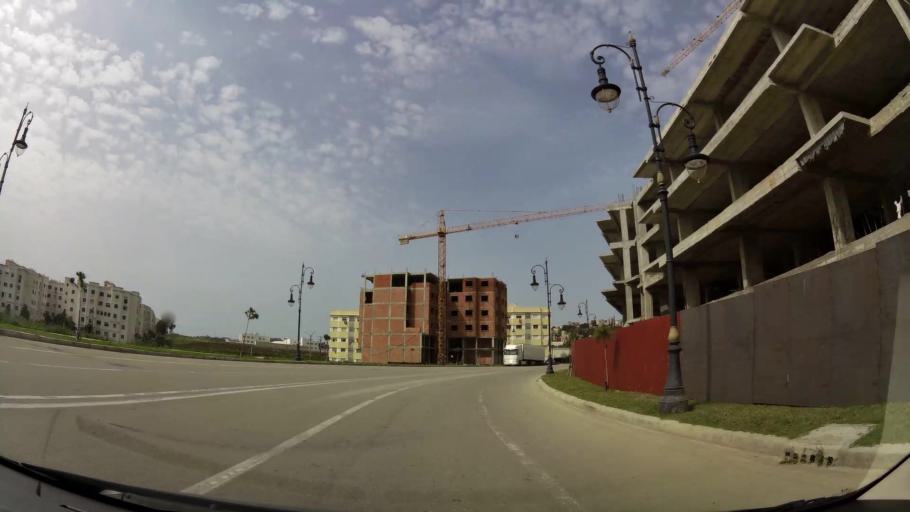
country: MA
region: Tanger-Tetouan
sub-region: Tanger-Assilah
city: Boukhalef
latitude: 35.7350
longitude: -5.8743
